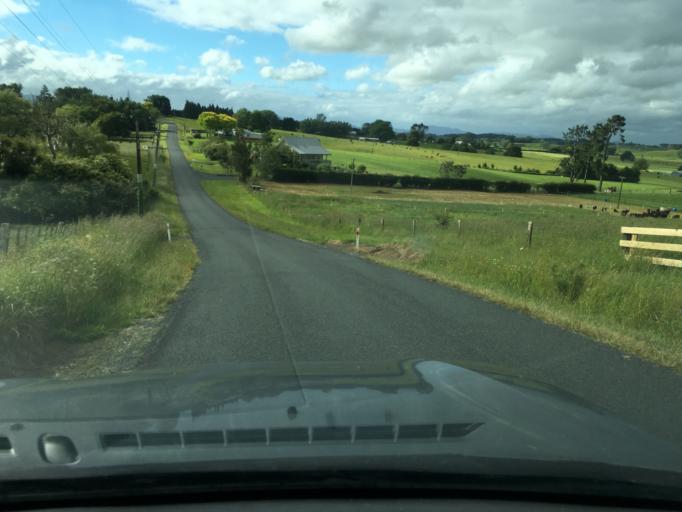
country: NZ
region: Waikato
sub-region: Hamilton City
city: Hamilton
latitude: -37.8281
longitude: 175.1798
